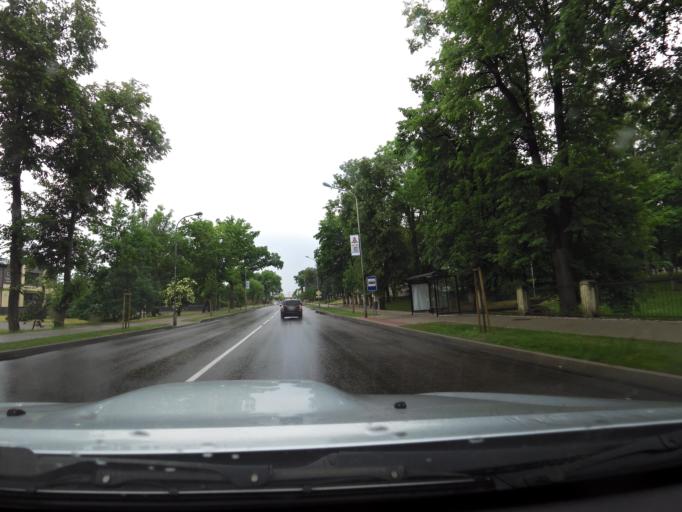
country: LT
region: Marijampoles apskritis
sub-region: Marijampole Municipality
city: Marijampole
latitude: 54.5490
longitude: 23.3479
